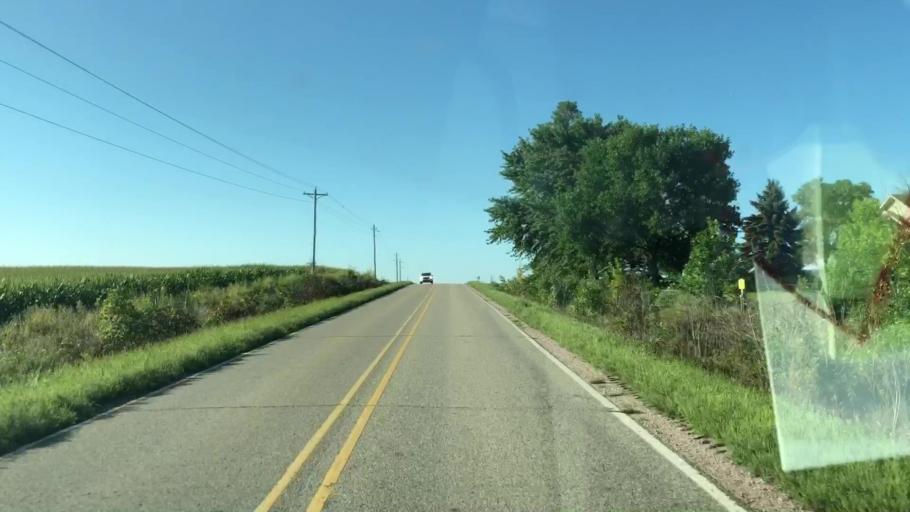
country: US
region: Iowa
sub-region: Woodbury County
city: Moville
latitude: 42.4621
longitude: -96.2138
